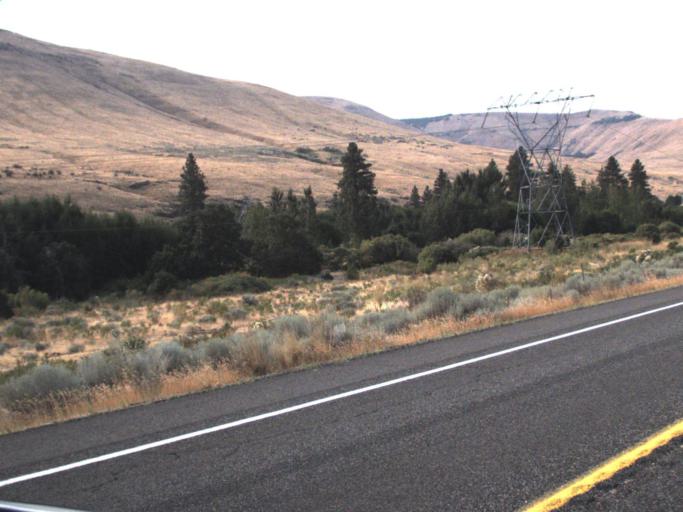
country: US
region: Washington
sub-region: Yakima County
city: Toppenish
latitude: 46.1045
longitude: -120.5425
